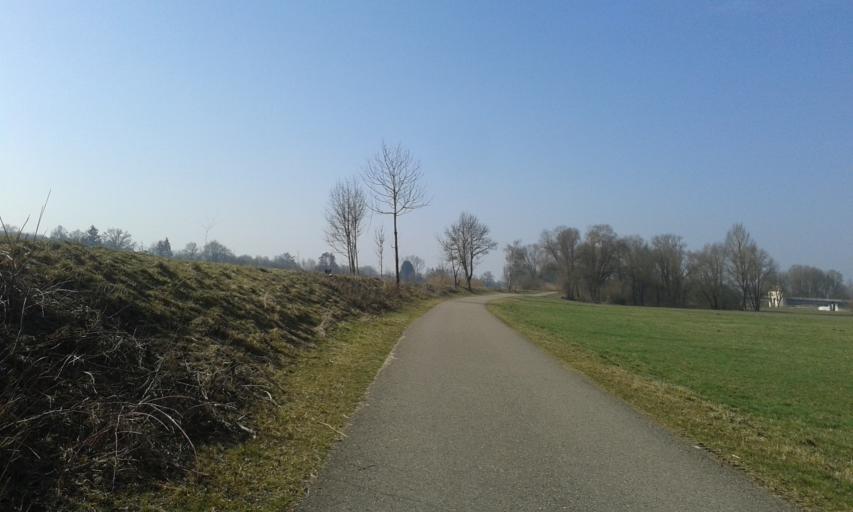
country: DE
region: Baden-Wuerttemberg
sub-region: Tuebingen Region
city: Ersingen
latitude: 48.3050
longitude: 9.8665
